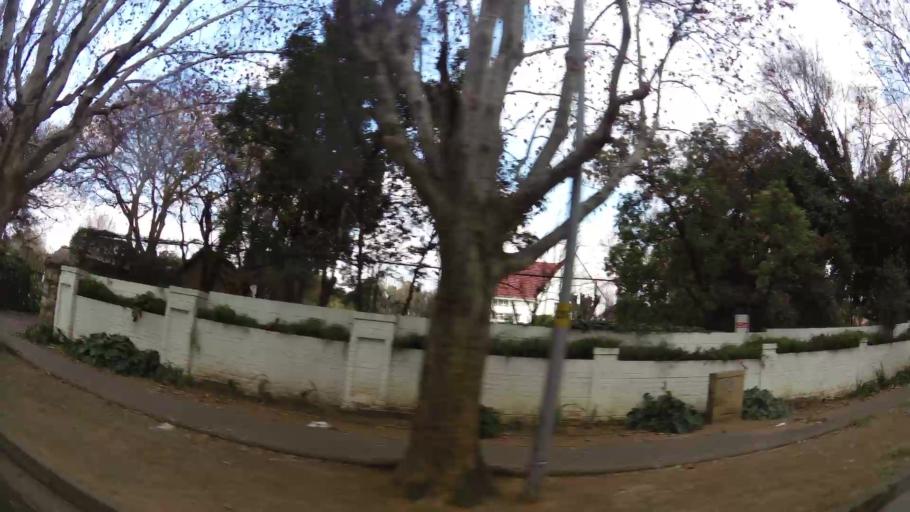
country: ZA
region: Gauteng
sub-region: Ekurhuleni Metropolitan Municipality
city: Germiston
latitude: -26.2348
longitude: 28.1717
